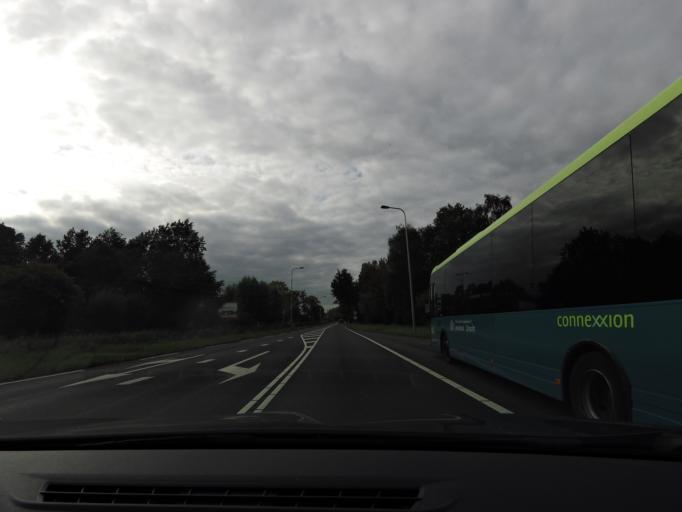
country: NL
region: Utrecht
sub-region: Gemeente Lopik
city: Lopik
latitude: 51.9724
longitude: 4.9580
